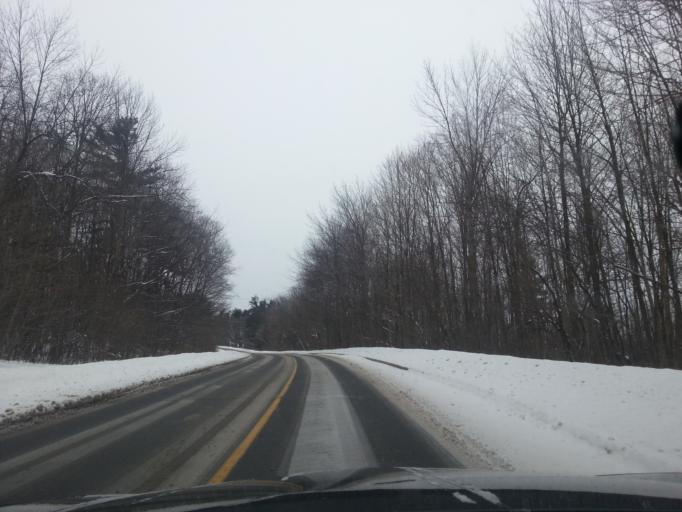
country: CA
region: Ontario
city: Ottawa
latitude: 45.4273
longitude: -75.7468
